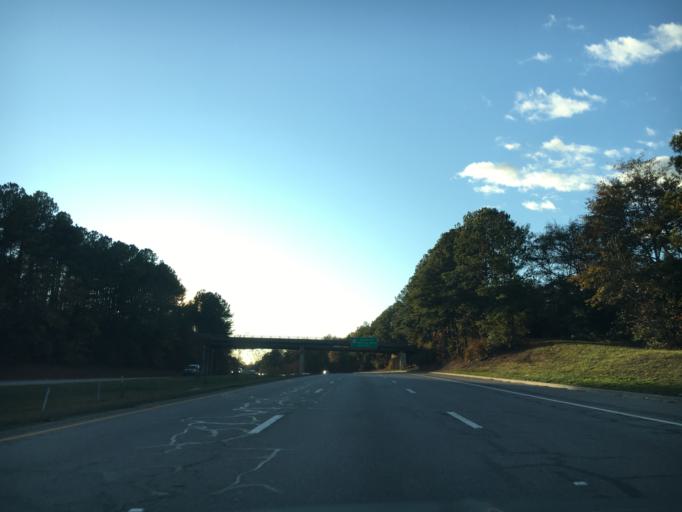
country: US
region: South Carolina
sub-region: Richland County
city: Columbia
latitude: 34.0344
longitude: -81.0274
